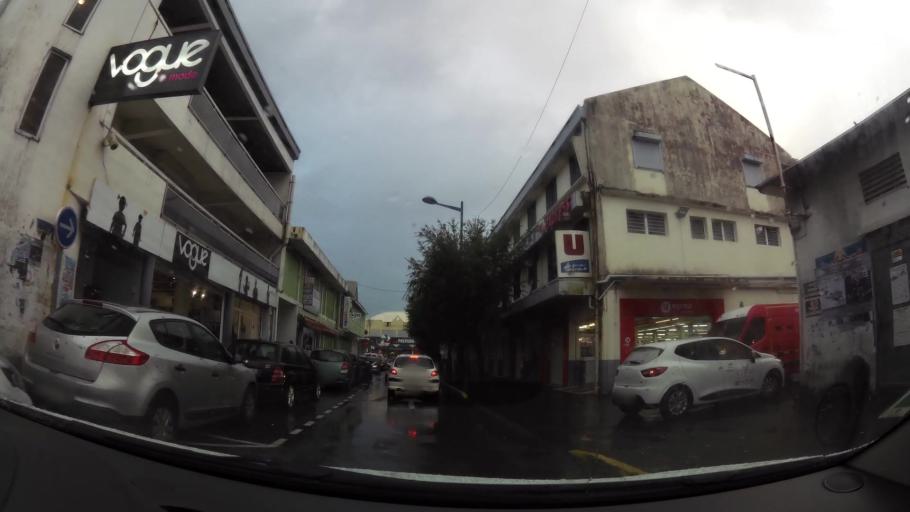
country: RE
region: Reunion
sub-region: Reunion
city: Saint-Benoit
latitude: -21.0349
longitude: 55.7133
